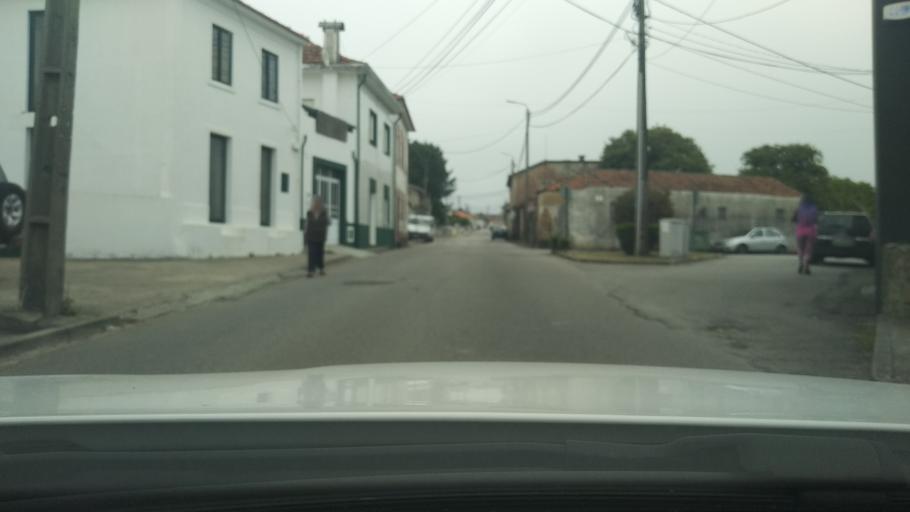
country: PT
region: Aveiro
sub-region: Espinho
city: Souto
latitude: 40.9872
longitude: -8.6232
